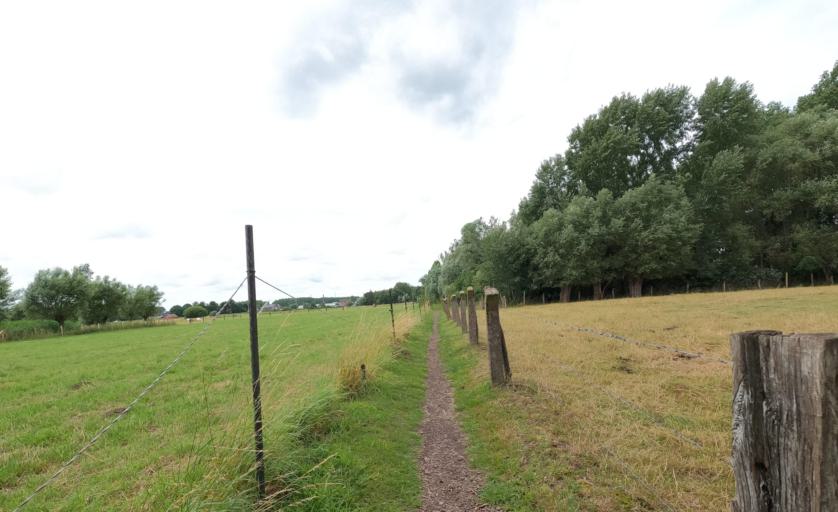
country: BE
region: Flanders
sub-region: Provincie Oost-Vlaanderen
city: Dendermonde
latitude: 51.0129
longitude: 4.1015
